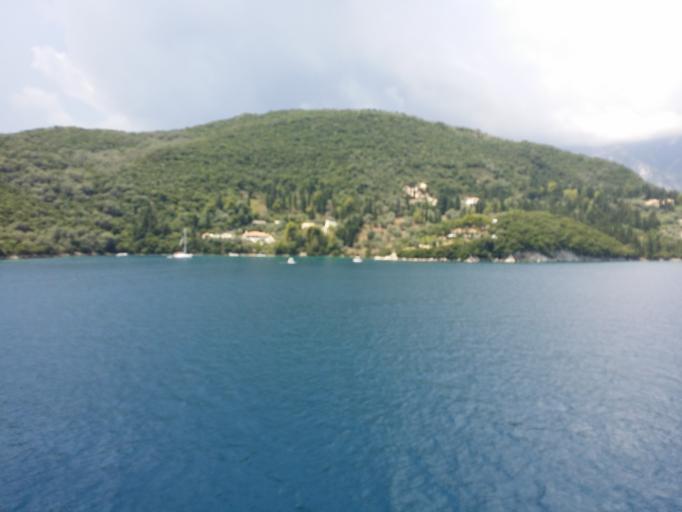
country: GR
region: Ionian Islands
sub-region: Lefkada
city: Nidri
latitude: 38.6981
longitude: 20.7255
